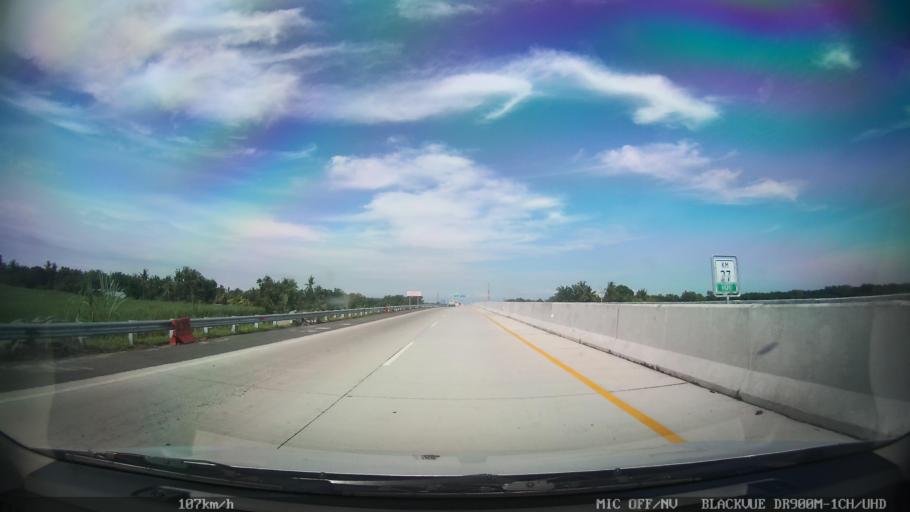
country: ID
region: North Sumatra
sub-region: Kabupaten Langkat
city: Stabat
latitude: 3.7134
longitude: 98.5122
